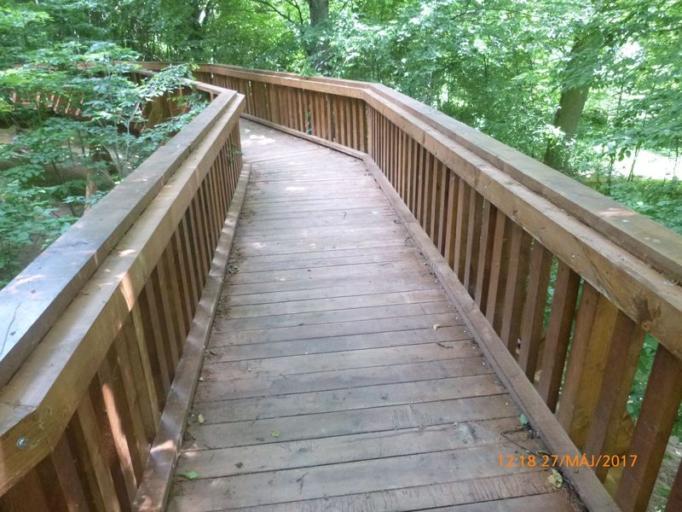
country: HU
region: Baranya
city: Buekkoesd
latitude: 46.1212
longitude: 18.0704
